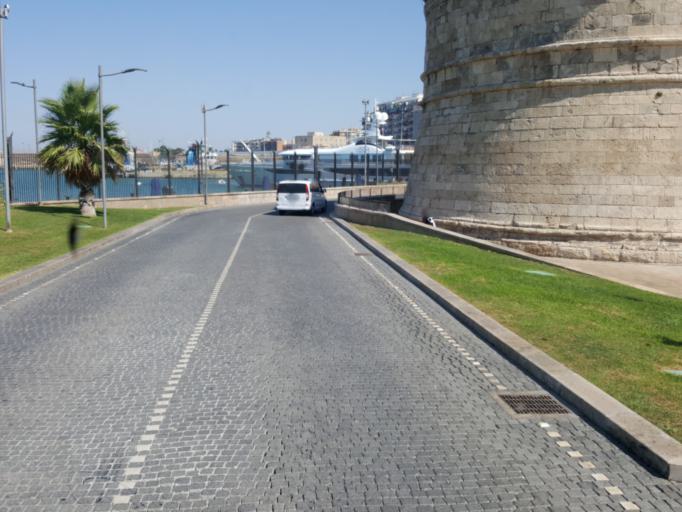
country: IT
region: Latium
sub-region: Citta metropolitana di Roma Capitale
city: Civitavecchia
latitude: 42.0899
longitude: 11.7899
